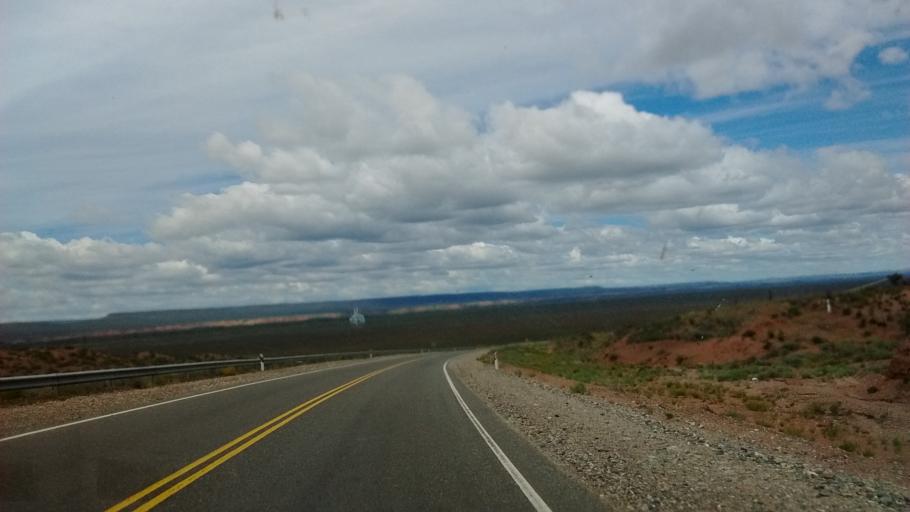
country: AR
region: Neuquen
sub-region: Departamento de Picun Leufu
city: Picun Leufu
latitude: -39.7789
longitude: -69.6547
